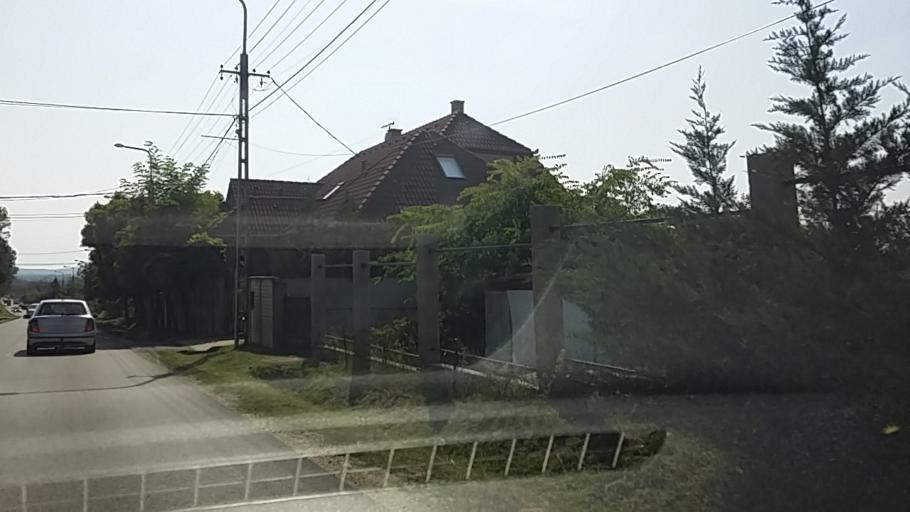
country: HU
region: Pest
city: Erdokertes
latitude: 47.6665
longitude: 19.3013
